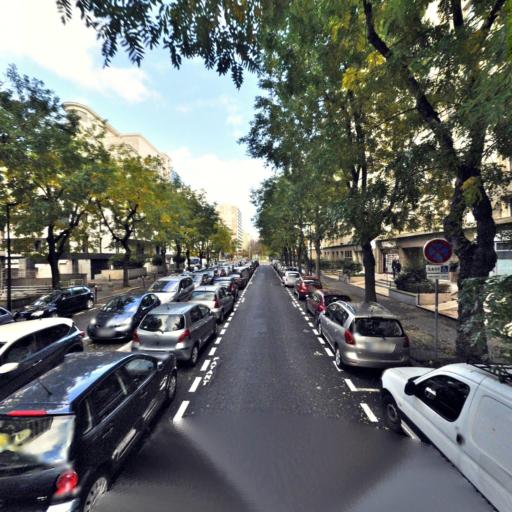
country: FR
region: Ile-de-France
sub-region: Departement des Hauts-de-Seine
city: Sevres
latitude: 48.8325
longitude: 2.2281
